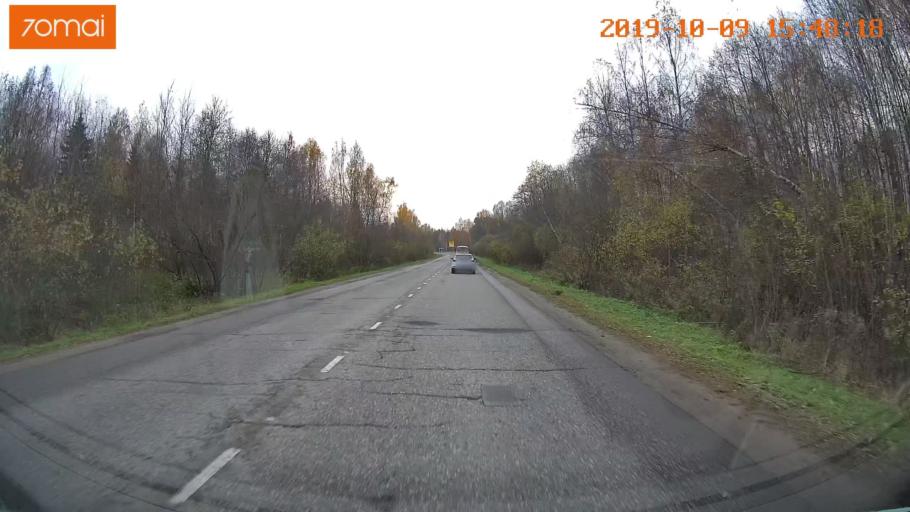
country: RU
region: Kostroma
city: Oktyabr'skiy
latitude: 57.8125
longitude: 41.0171
